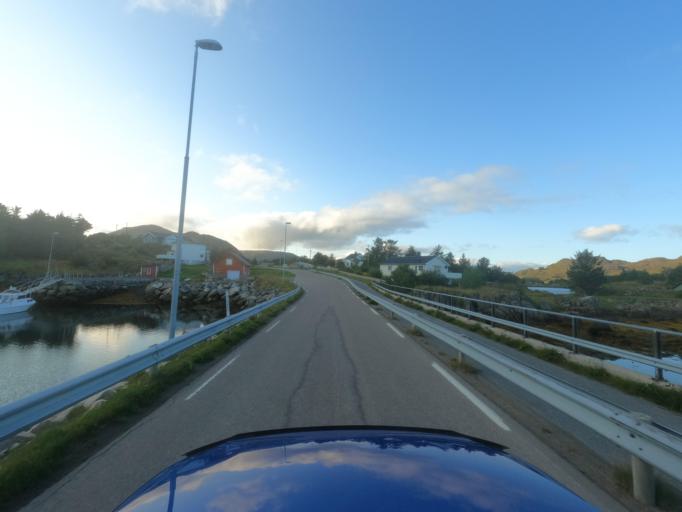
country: NO
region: Nordland
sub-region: Vestvagoy
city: Gravdal
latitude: 68.0796
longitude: 13.5462
